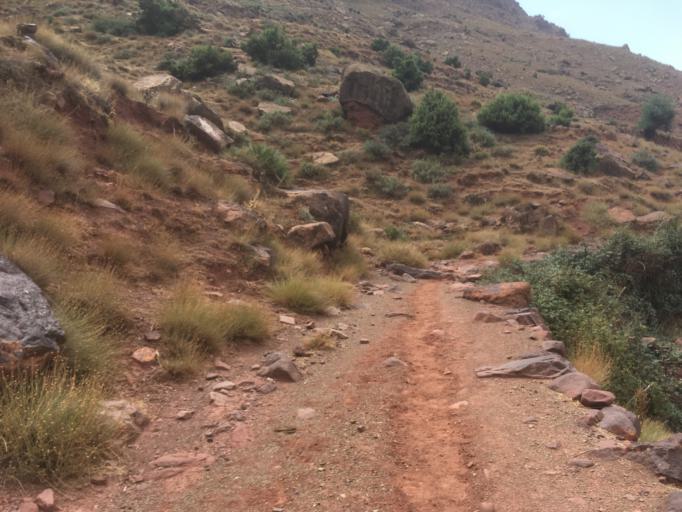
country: MA
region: Marrakech-Tensift-Al Haouz
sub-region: Al-Haouz
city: Tidili Mesfioua
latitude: 31.2946
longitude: -7.6696
